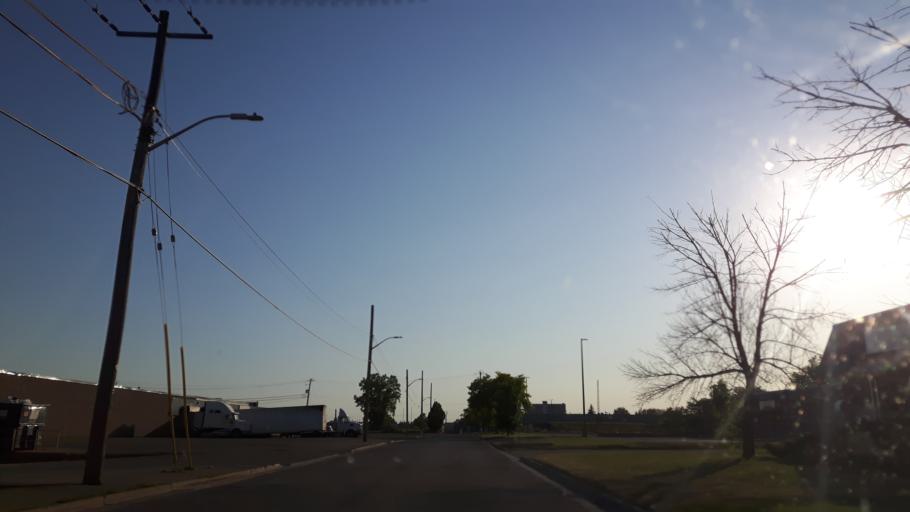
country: CA
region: Ontario
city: London
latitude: 42.9337
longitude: -81.2144
